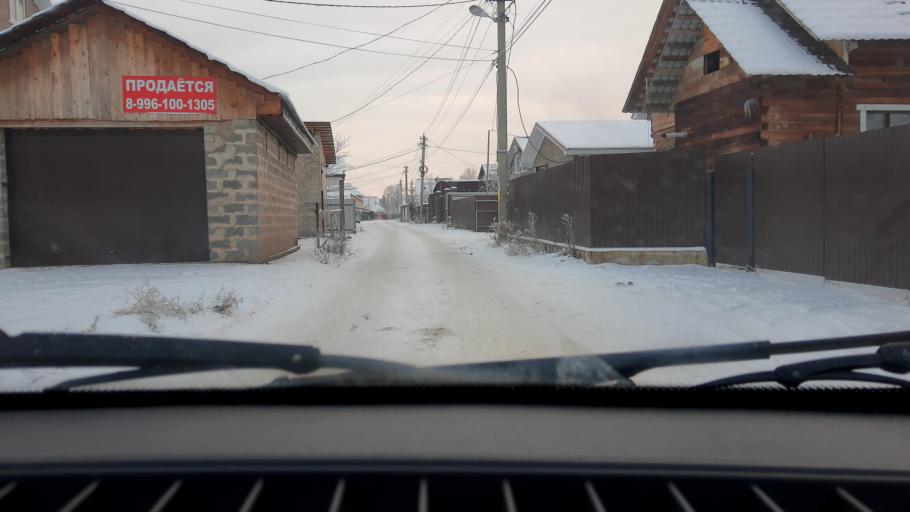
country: RU
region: Bashkortostan
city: Ufa
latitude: 54.6595
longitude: 55.9248
